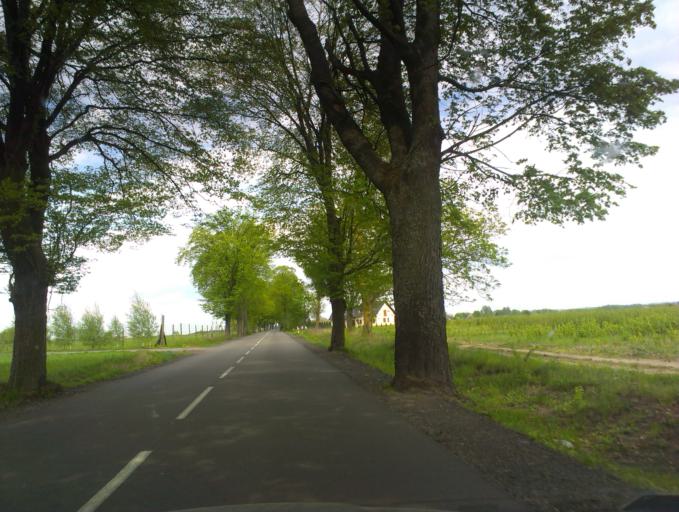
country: PL
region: Pomeranian Voivodeship
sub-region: Powiat czluchowski
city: Czarne
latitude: 53.6843
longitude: 16.9598
